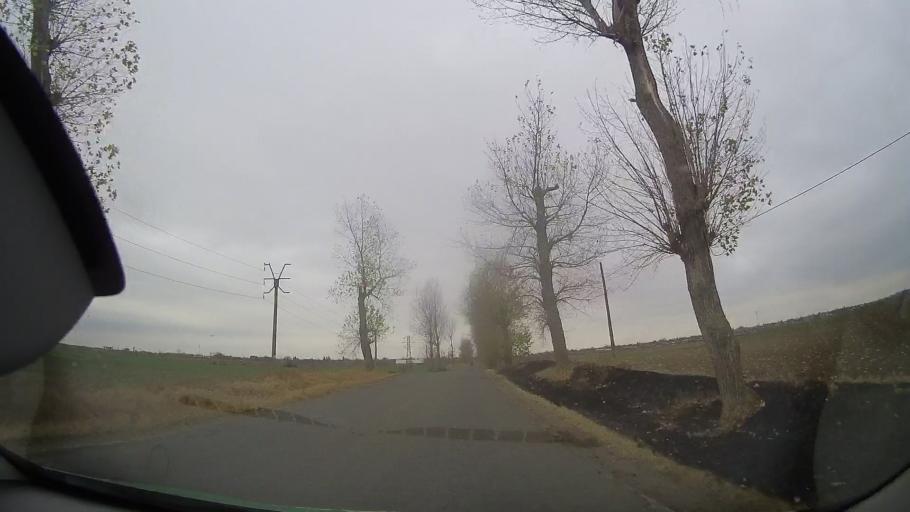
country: RO
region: Buzau
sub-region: Comuna Rusetu
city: Rusetu
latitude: 44.9502
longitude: 27.2257
